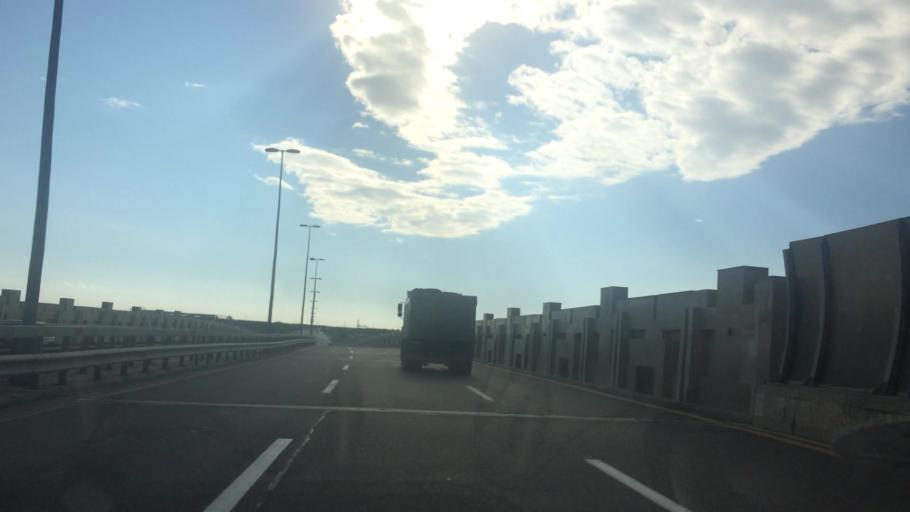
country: AZ
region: Baki
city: Hovsan
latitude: 40.3913
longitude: 50.0727
